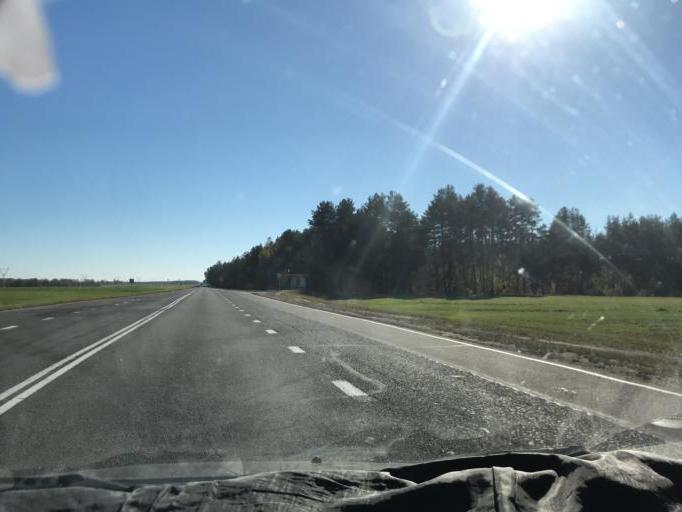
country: BY
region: Gomel
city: Parychy
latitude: 52.8701
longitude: 29.3207
